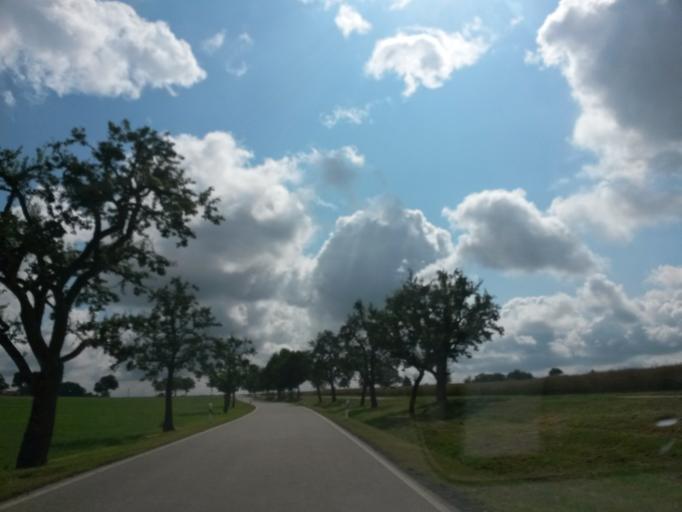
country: DE
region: Baden-Wuerttemberg
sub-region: Regierungsbezirk Stuttgart
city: Ellwangen
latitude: 48.9696
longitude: 10.1596
